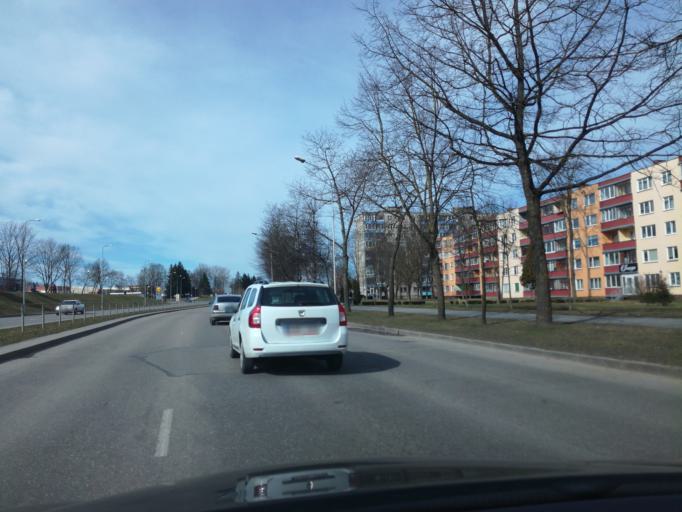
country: LT
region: Alytaus apskritis
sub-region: Alytus
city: Alytus
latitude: 54.3987
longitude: 24.0259
